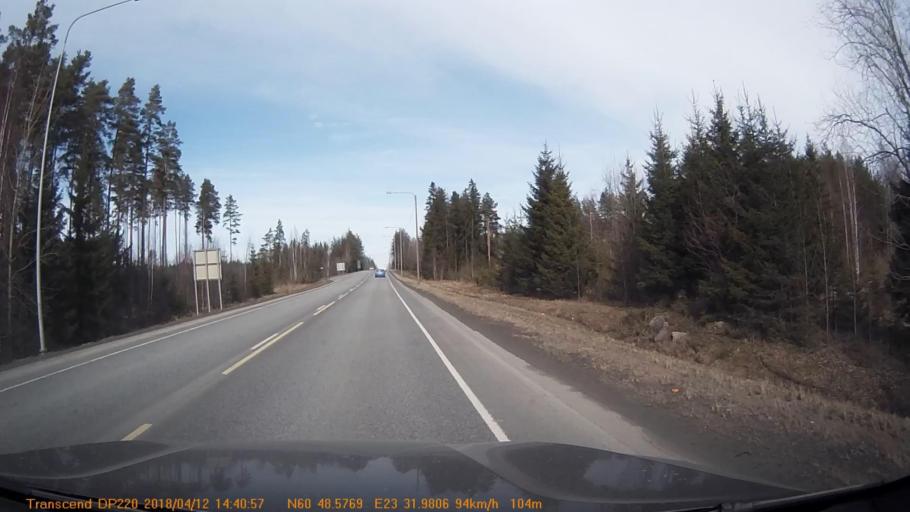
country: FI
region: Haeme
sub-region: Forssa
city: Jokioinen
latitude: 60.8098
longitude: 23.5334
